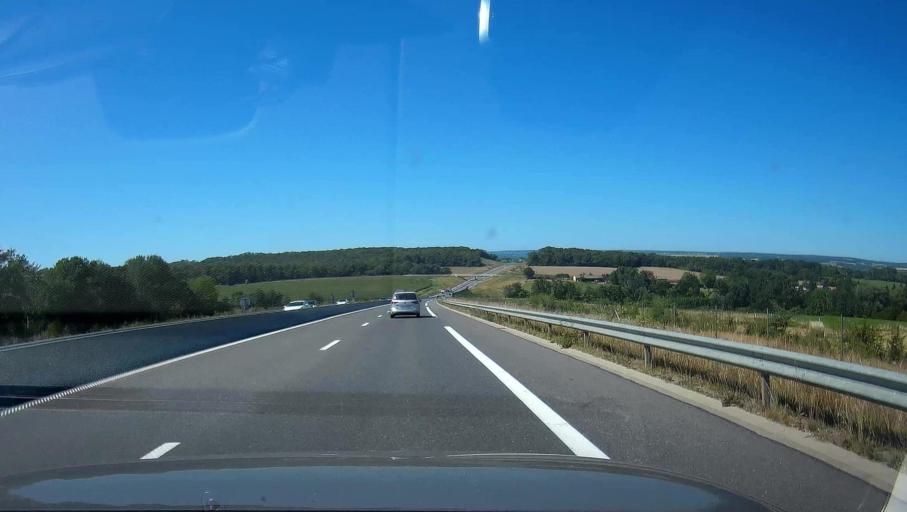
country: FR
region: Champagne-Ardenne
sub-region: Departement des Ardennes
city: Prix-les-Mezieres
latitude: 49.7476
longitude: 4.6669
